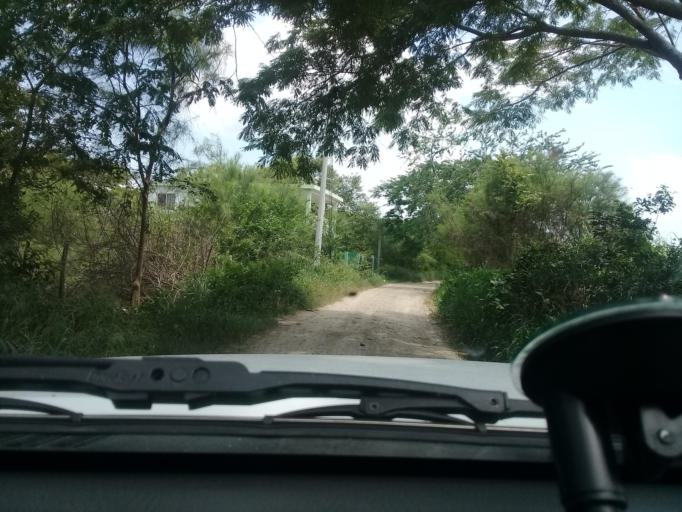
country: MX
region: Veracruz
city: Moralillo
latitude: 22.1789
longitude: -98.0170
